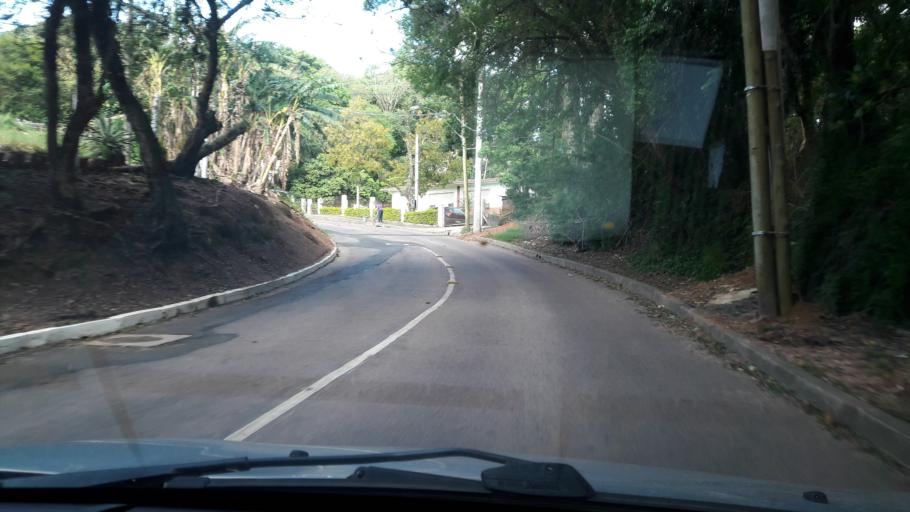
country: BR
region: Rio Grande do Sul
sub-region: Porto Alegre
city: Porto Alegre
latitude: -30.0852
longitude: -51.2004
